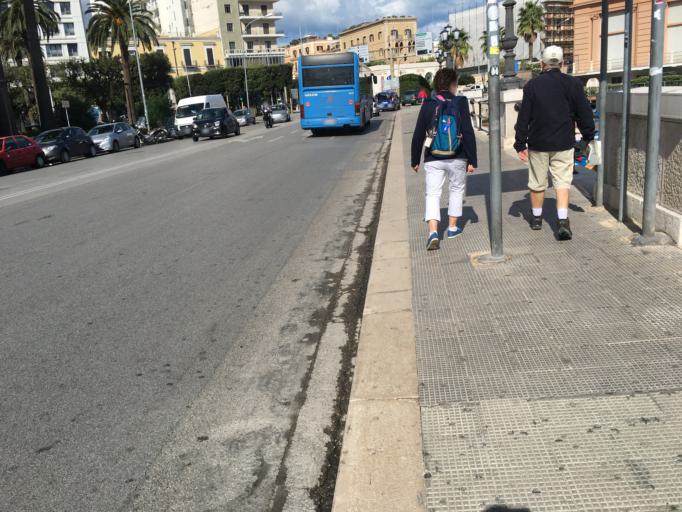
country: IT
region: Apulia
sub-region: Provincia di Bari
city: Bari
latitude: 41.1256
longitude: 16.8732
